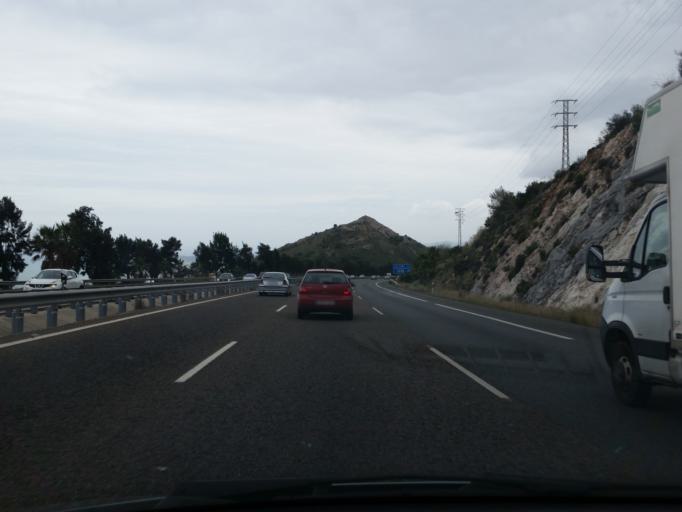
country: ES
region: Andalusia
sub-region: Provincia de Malaga
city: Benalmadena
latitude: 36.5915
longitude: -4.5814
